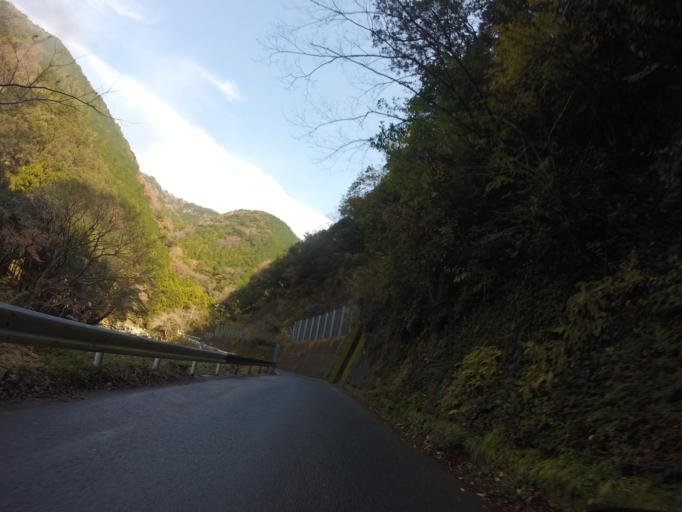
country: JP
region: Shizuoka
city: Heda
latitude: 34.8055
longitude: 138.8111
